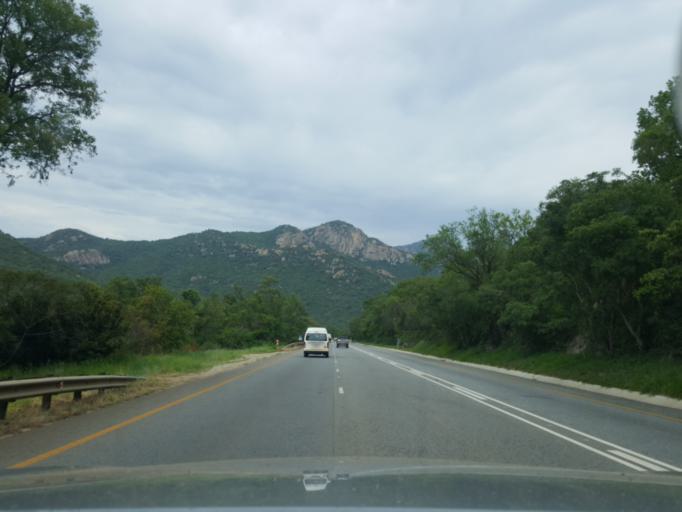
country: ZA
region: Mpumalanga
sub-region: Ehlanzeni District
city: Nelspruit
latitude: -25.5262
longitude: 31.2655
